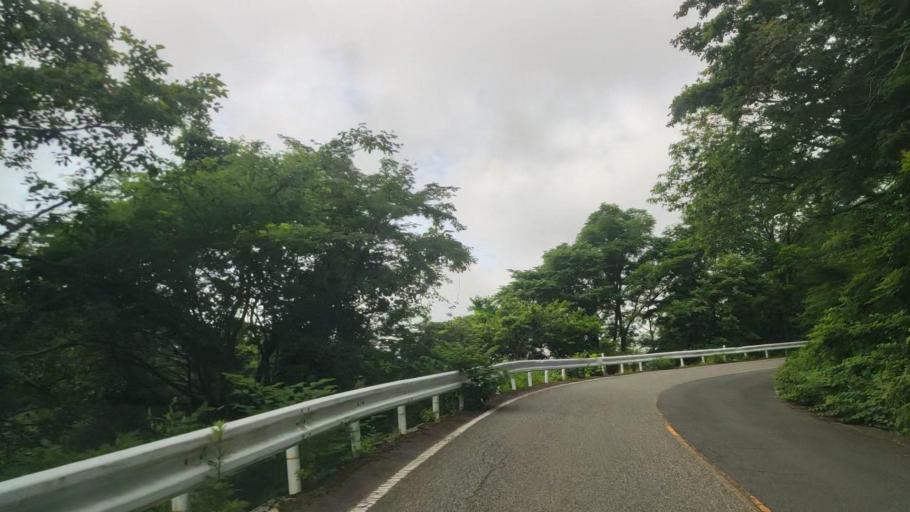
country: JP
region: Tottori
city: Yonago
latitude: 35.3373
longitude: 133.5575
